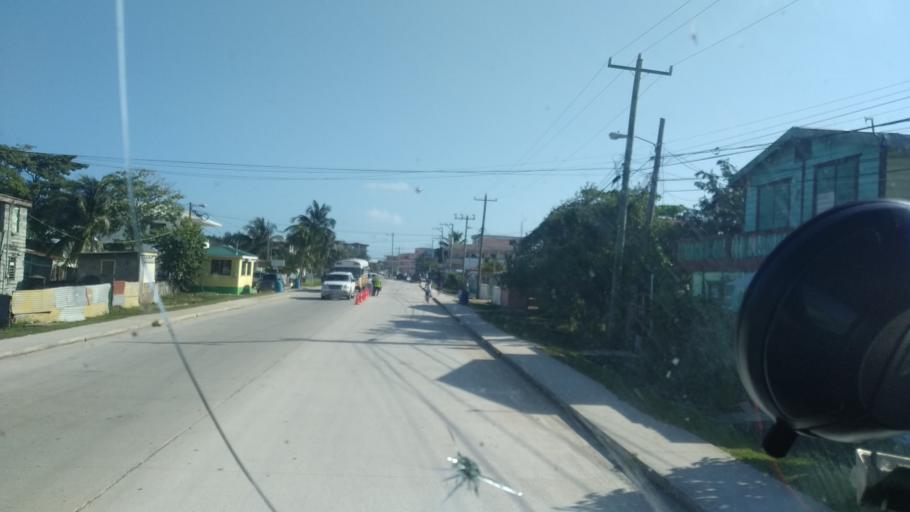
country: BZ
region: Belize
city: Belize City
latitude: 17.4870
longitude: -88.2016
